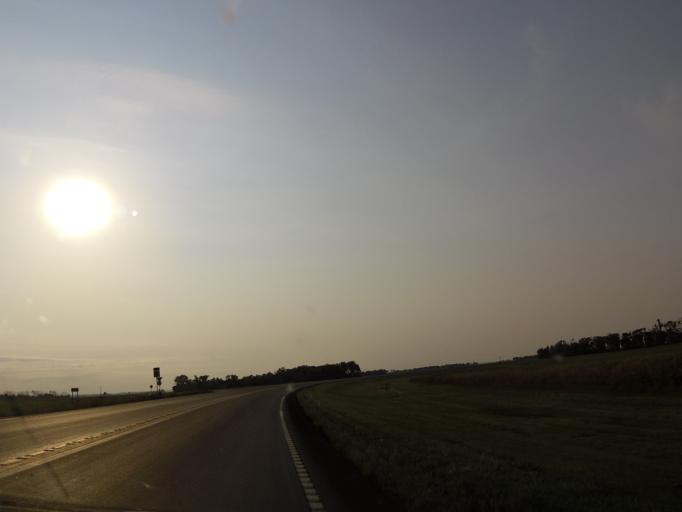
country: US
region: North Dakota
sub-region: Traill County
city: Mayville
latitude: 47.3531
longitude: -97.3190
